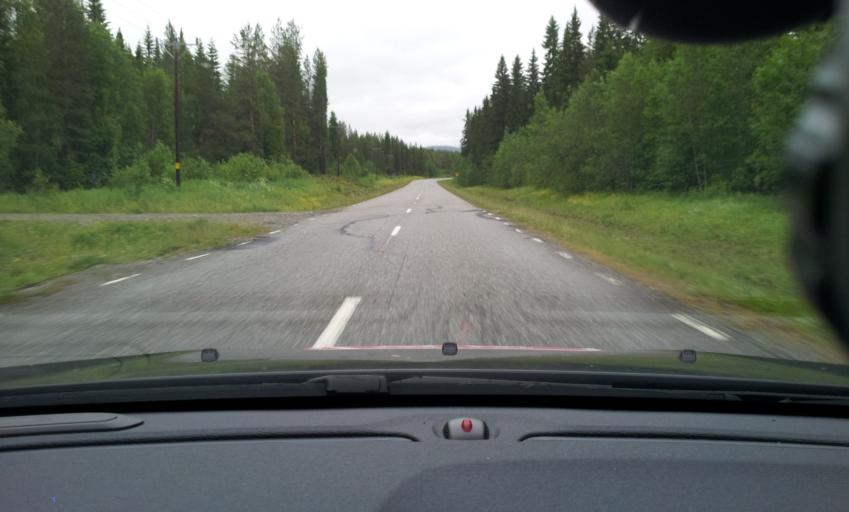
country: SE
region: Jaemtland
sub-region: Ragunda Kommun
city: Hammarstrand
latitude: 63.2860
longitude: 15.7868
